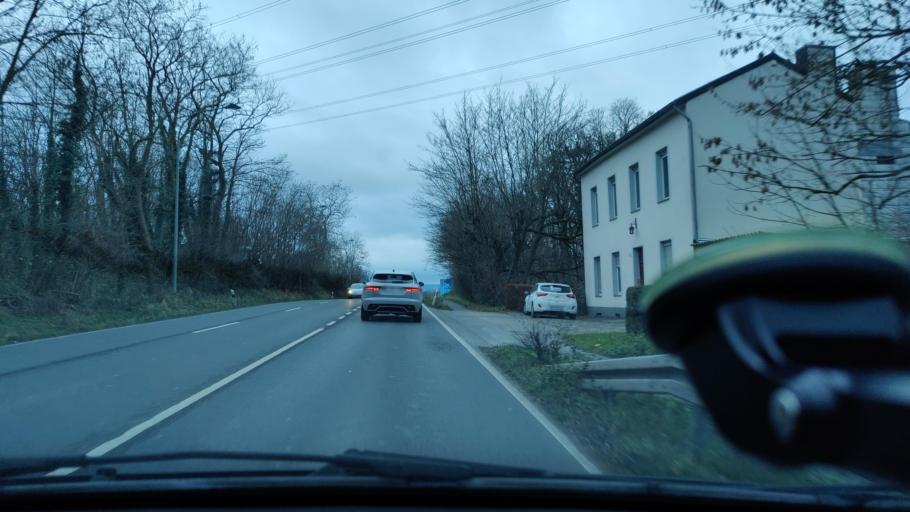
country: DE
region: North Rhine-Westphalia
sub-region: Regierungsbezirk Koln
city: Wurselen
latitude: 50.8091
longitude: 6.1144
